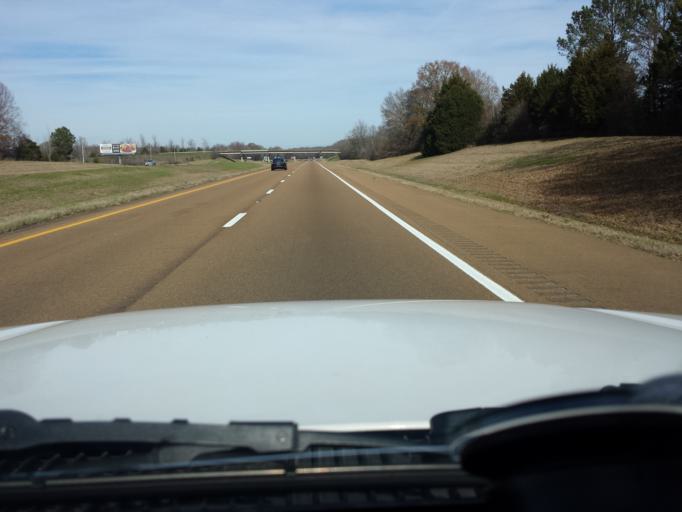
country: US
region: Mississippi
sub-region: Madison County
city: Canton
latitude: 32.6653
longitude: -90.0610
